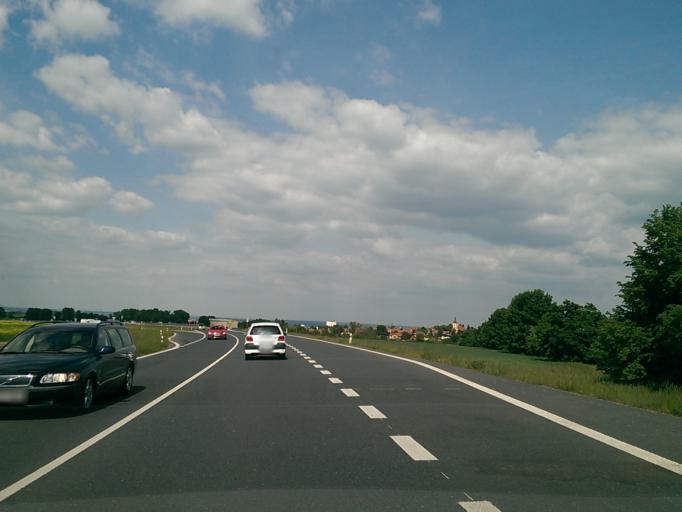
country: CZ
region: Central Bohemia
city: Libeznice
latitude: 50.1871
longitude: 14.4808
